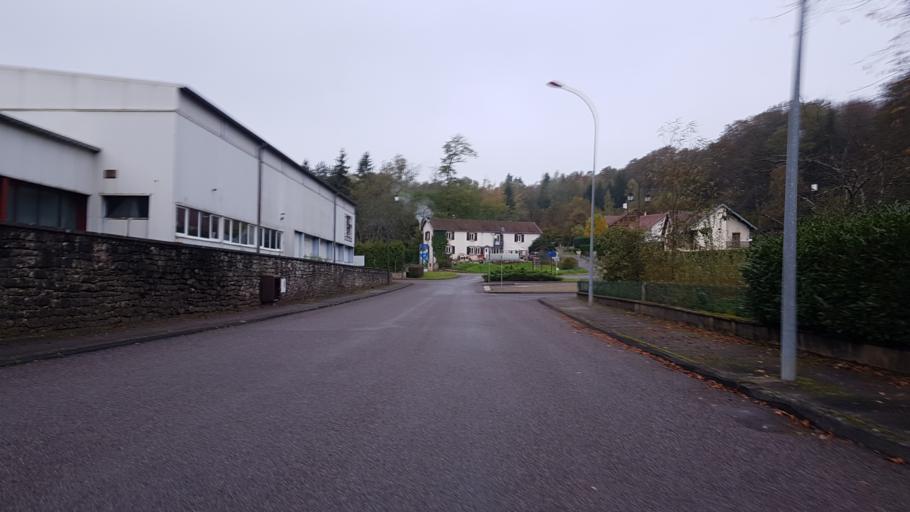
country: FR
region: Franche-Comte
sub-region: Departement de la Haute-Saone
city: Luxeuil-les-Bains
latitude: 47.8258
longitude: 6.3673
